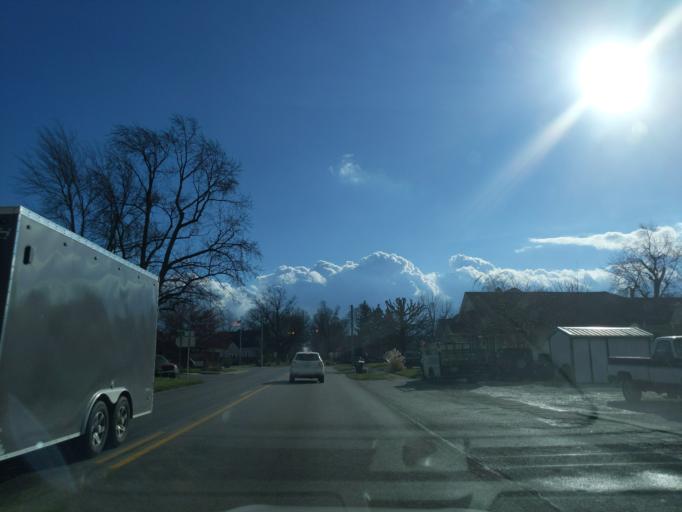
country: US
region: Indiana
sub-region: Decatur County
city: Greensburg
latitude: 39.3422
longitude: -85.4898
